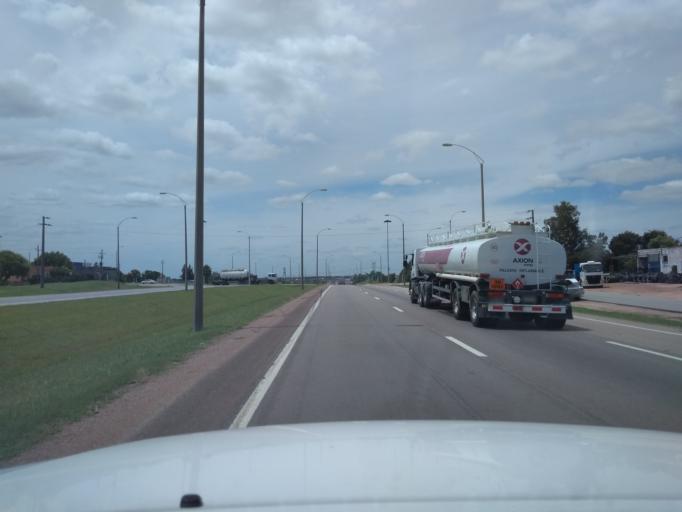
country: UY
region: Canelones
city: La Paz
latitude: -34.7686
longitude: -56.2669
